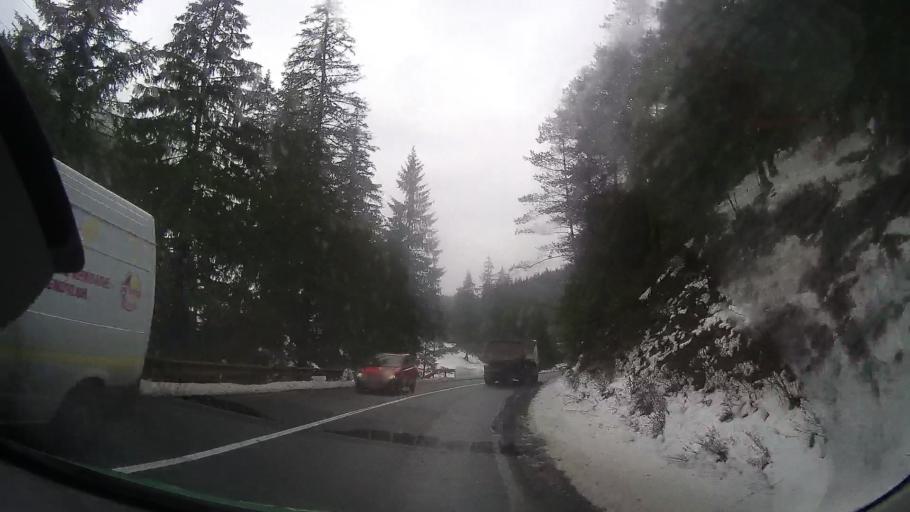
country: RO
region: Neamt
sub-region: Comuna Bicaz Chei
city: Bicaz Chei
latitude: 46.7783
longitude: 25.7610
